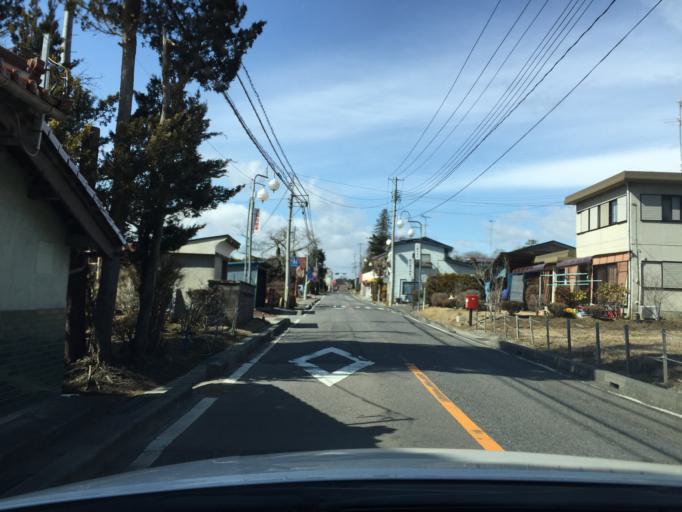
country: JP
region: Fukushima
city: Funehikimachi-funehiki
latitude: 37.3958
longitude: 140.5720
